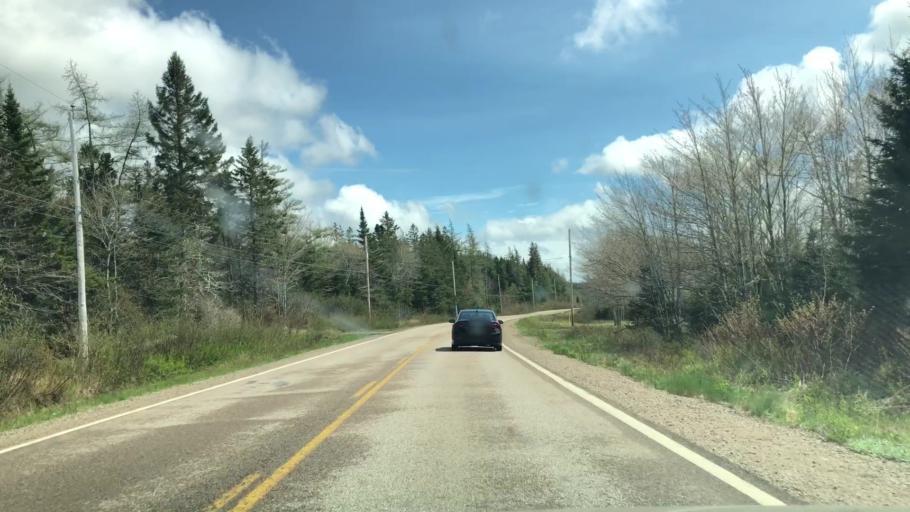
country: CA
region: Nova Scotia
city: Antigonish
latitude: 45.2103
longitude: -62.0042
